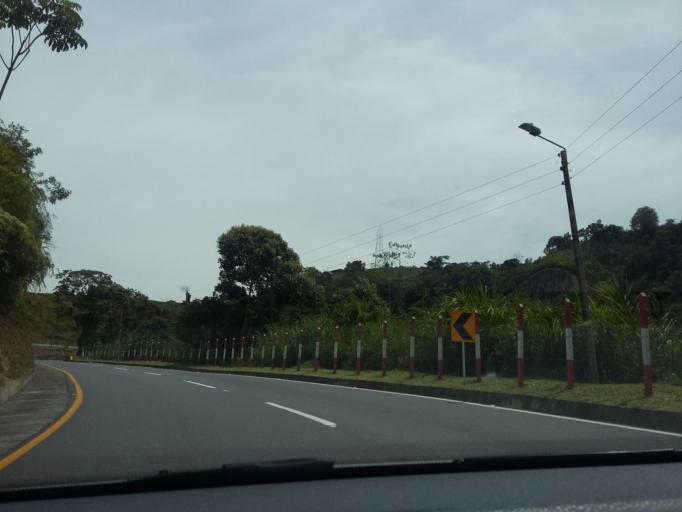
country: CO
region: Santander
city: Bucaramanga
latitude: 7.1156
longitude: -73.0787
